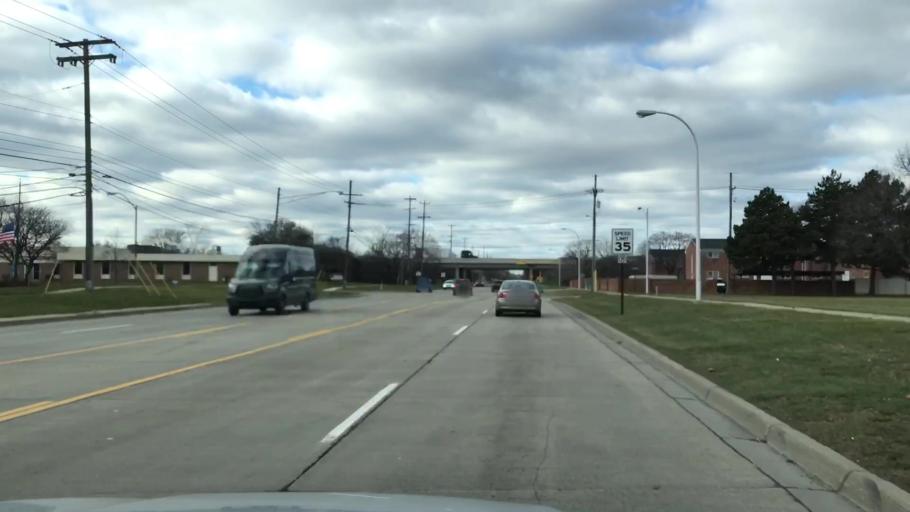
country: US
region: Michigan
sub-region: Oakland County
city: Madison Heights
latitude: 42.5200
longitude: -83.1125
